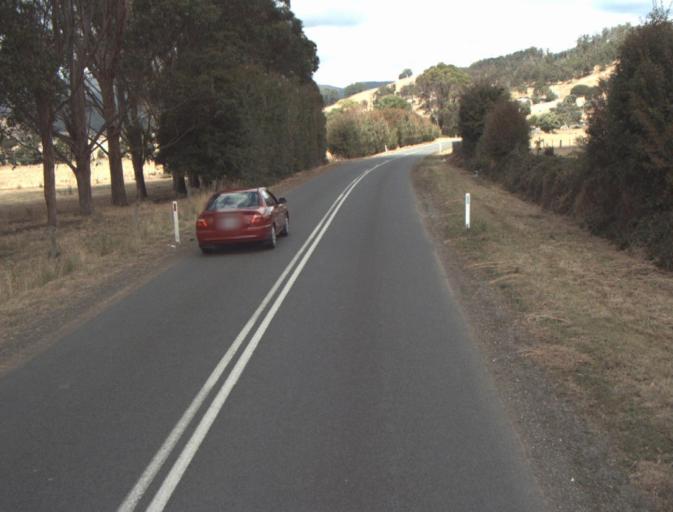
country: AU
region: Tasmania
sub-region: Launceston
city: Mayfield
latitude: -41.2296
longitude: 147.1235
